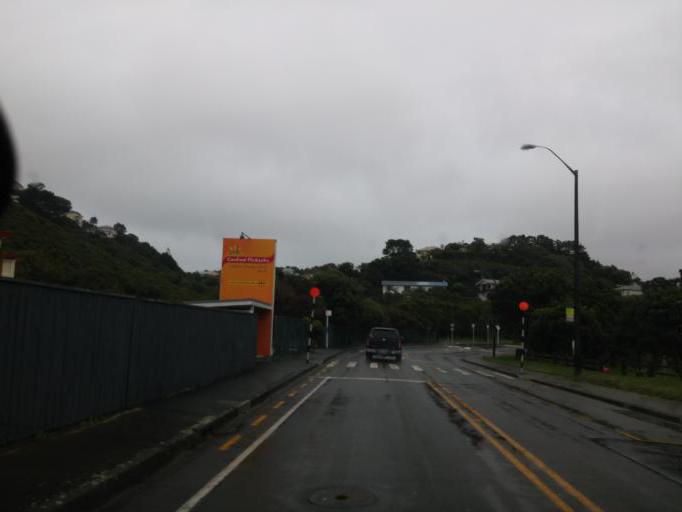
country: NZ
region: Wellington
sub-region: Wellington City
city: Kelburn
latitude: -41.2751
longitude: 174.7561
